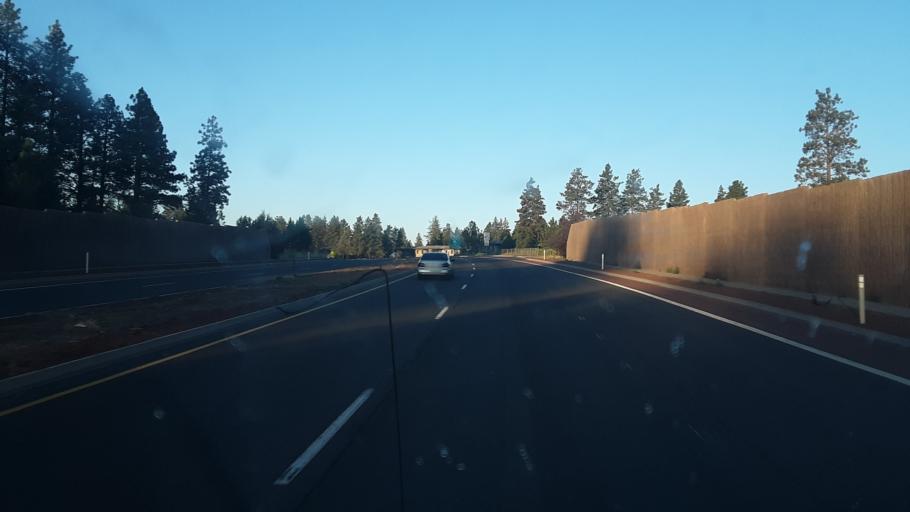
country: US
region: Oregon
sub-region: Deschutes County
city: Bend
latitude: 44.0363
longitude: -121.3117
